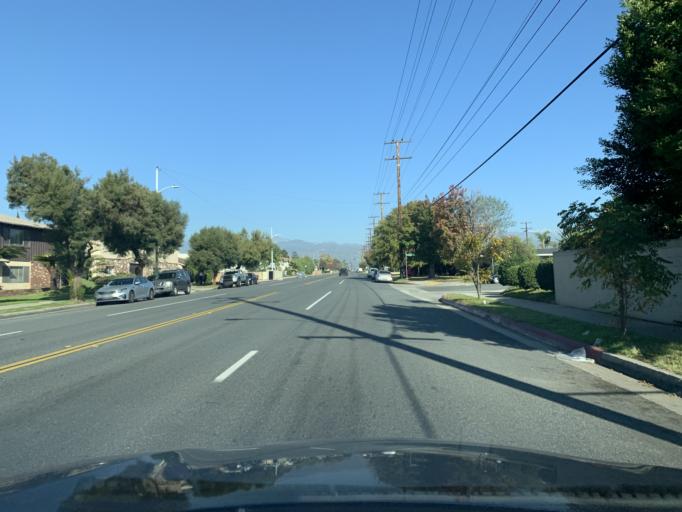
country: US
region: California
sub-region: Los Angeles County
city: Covina
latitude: 34.0807
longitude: -117.8813
